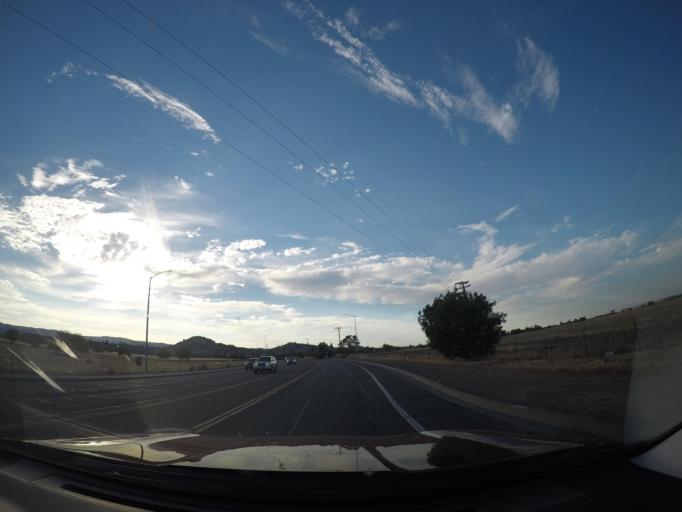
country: US
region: California
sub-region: Solano County
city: Vacaville
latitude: 38.3682
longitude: -121.9695
